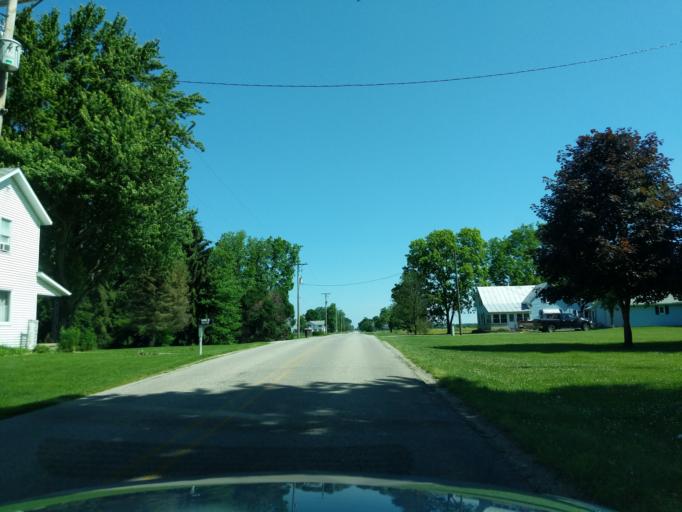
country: US
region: Indiana
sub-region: Huntington County
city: Warren
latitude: 40.7513
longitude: -85.5070
